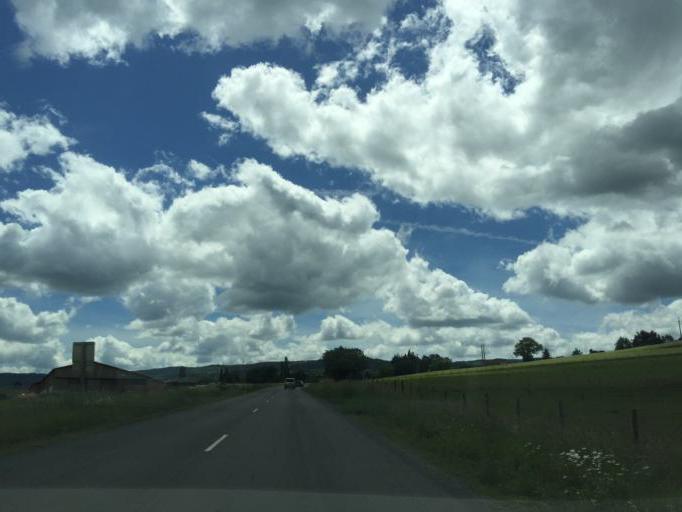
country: FR
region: Rhone-Alpes
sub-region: Departement de la Loire
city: Lezigneux
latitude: 45.5237
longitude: 4.0531
